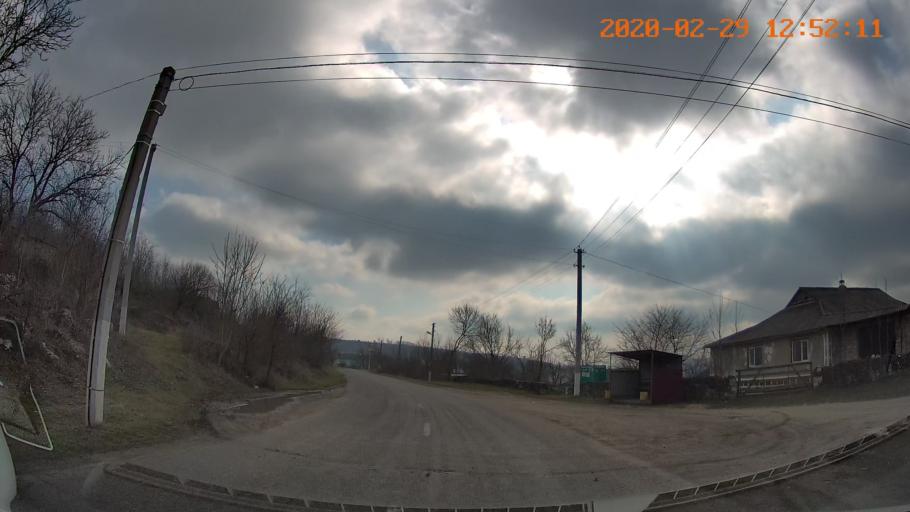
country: MD
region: Telenesti
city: Camenca
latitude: 48.1136
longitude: 28.7322
